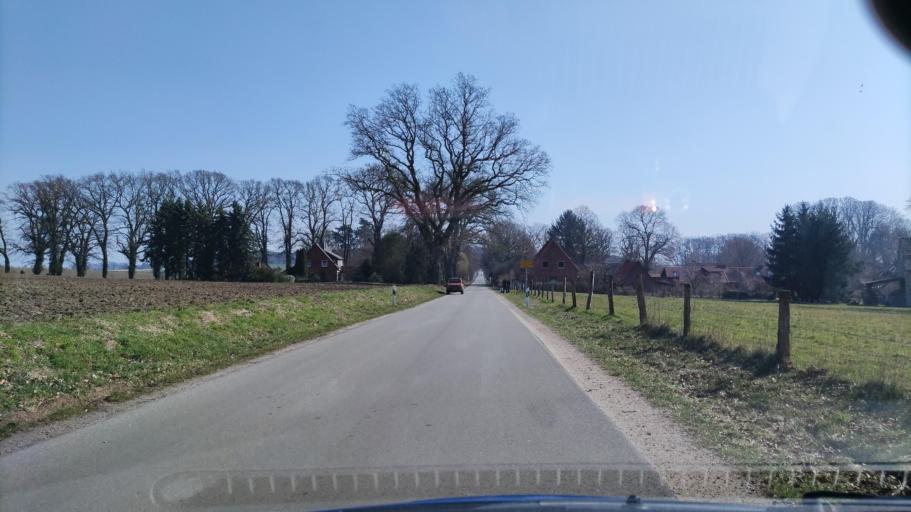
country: DE
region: Lower Saxony
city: Clenze
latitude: 52.9496
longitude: 10.9355
